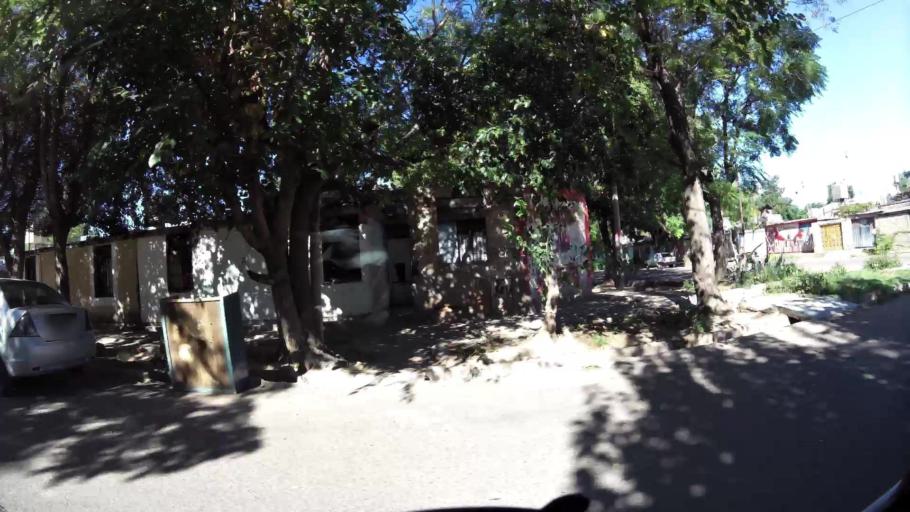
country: AR
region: Mendoza
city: Las Heras
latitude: -32.8428
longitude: -68.8234
